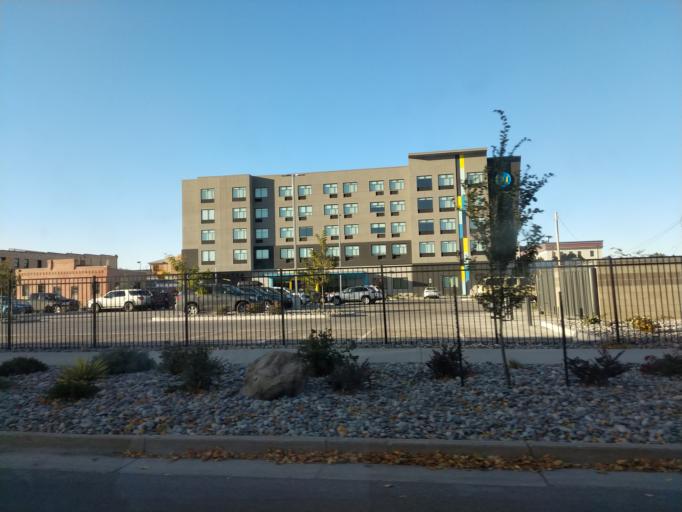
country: US
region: Colorado
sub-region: Mesa County
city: Grand Junction
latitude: 39.0654
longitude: -108.5685
